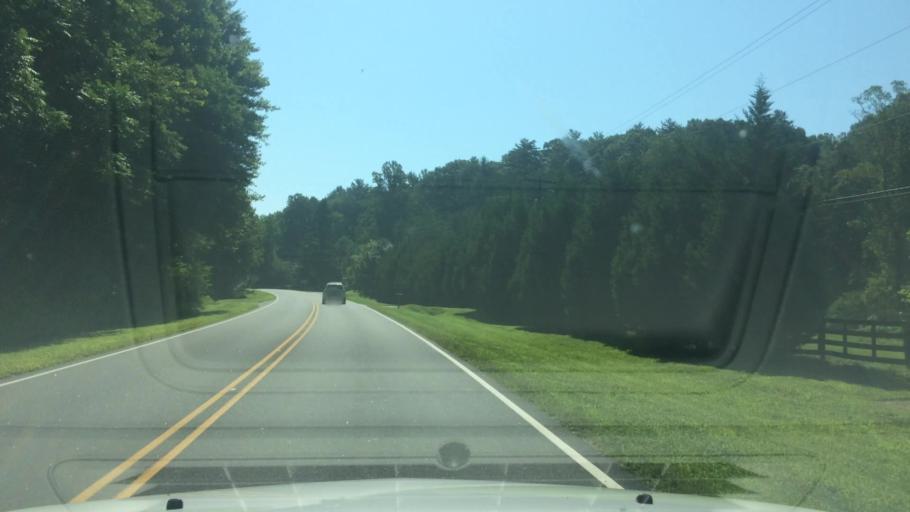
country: US
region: North Carolina
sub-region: Caldwell County
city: Lenoir
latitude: 35.9145
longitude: -81.4800
